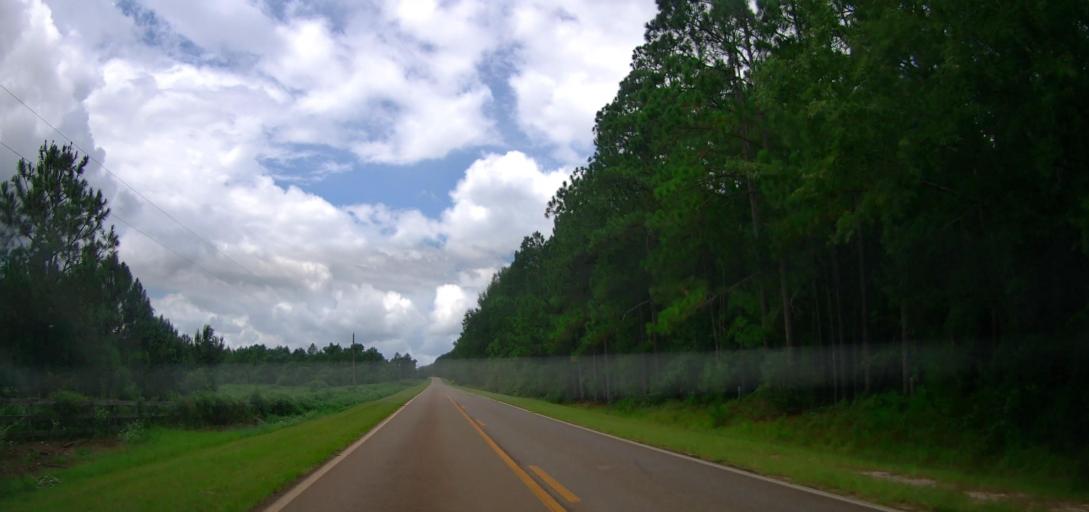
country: US
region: Georgia
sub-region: Pulaski County
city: Hawkinsville
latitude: 32.3384
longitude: -83.5451
